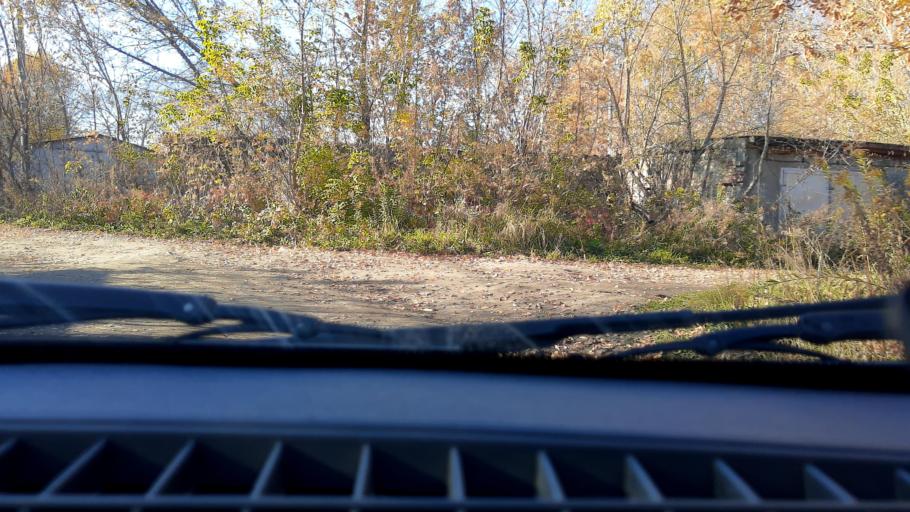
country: RU
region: Bashkortostan
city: Ufa
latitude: 54.8354
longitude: 56.1222
